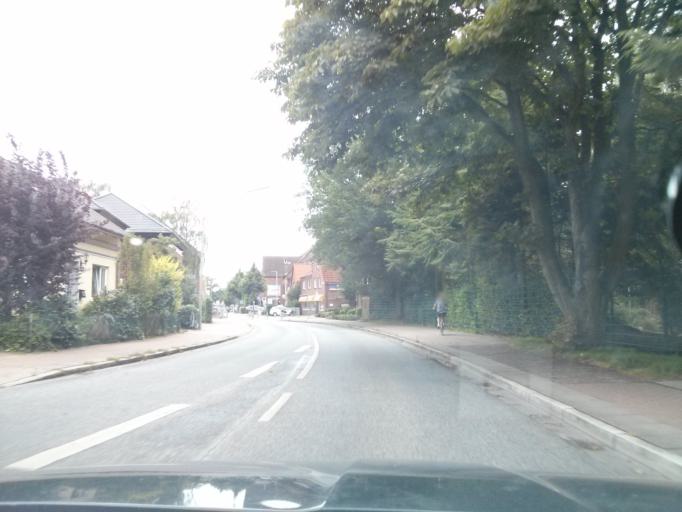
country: DE
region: Schleswig-Holstein
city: Wedel
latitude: 53.5814
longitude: 9.7626
